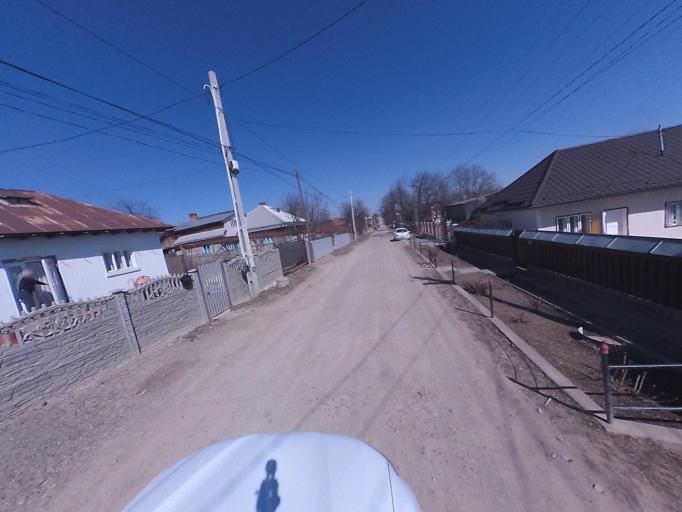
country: RO
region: Neamt
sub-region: Oras Targu Neamt
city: Humulesti
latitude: 47.1876
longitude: 26.3351
